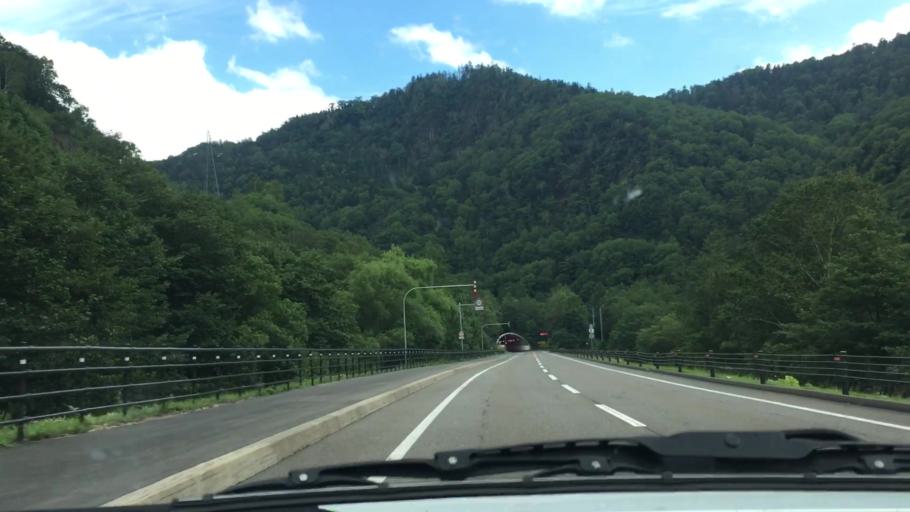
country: JP
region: Hokkaido
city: Otofuke
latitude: 43.3656
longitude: 143.2345
